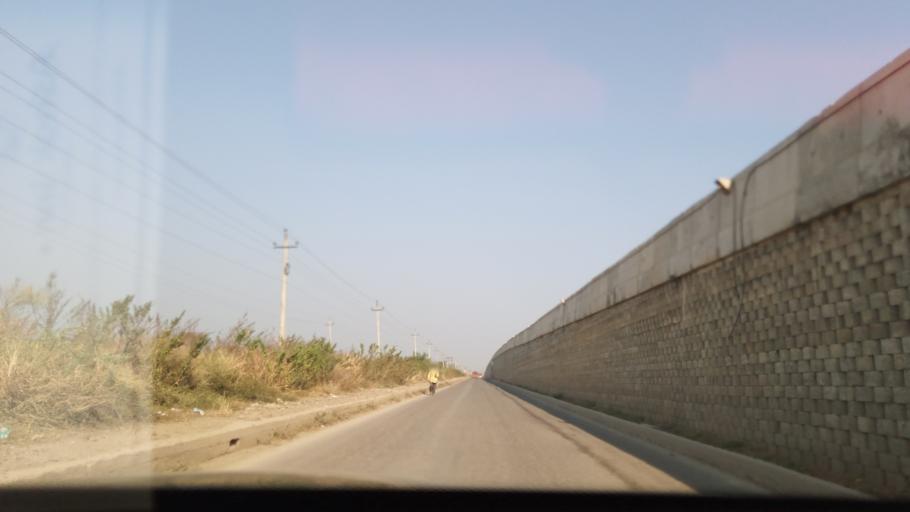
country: IN
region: Karnataka
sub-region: Haveri
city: Savanur
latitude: 14.8815
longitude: 75.3088
